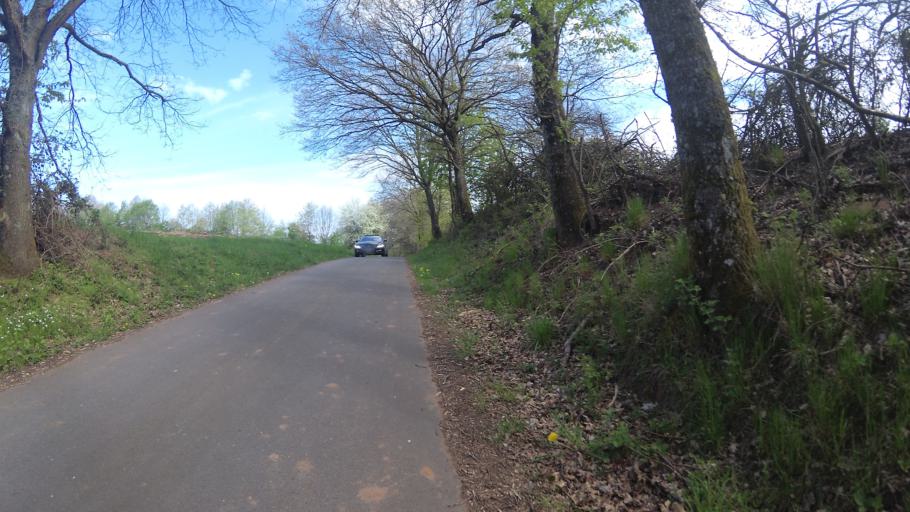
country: DE
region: Saarland
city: Mainzweiler
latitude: 49.4482
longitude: 7.1155
